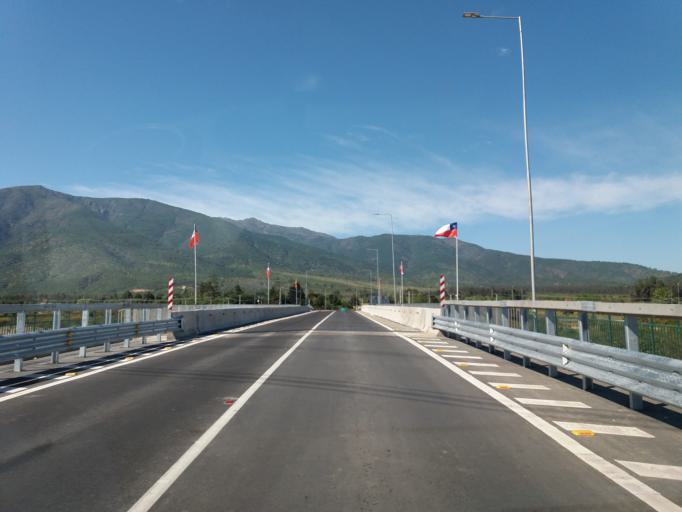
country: CL
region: Valparaiso
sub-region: Provincia de Marga Marga
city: Limache
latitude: -33.0178
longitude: -71.1715
